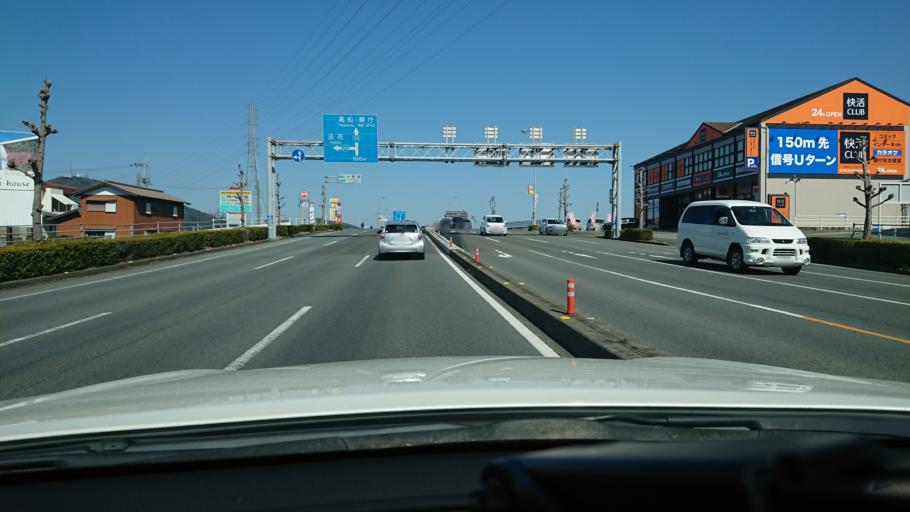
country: JP
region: Tokushima
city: Tokushima-shi
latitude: 34.0434
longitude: 134.5517
